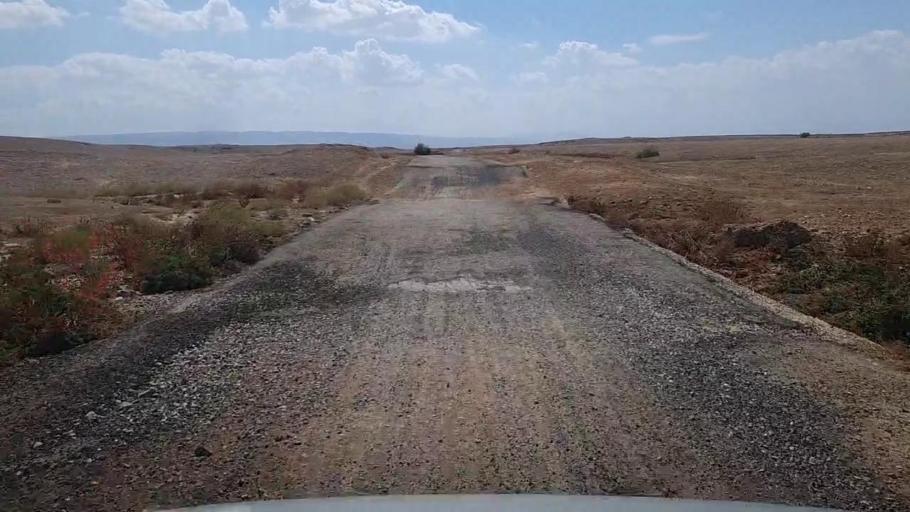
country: PK
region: Sindh
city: Bhan
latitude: 26.3807
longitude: 67.6350
